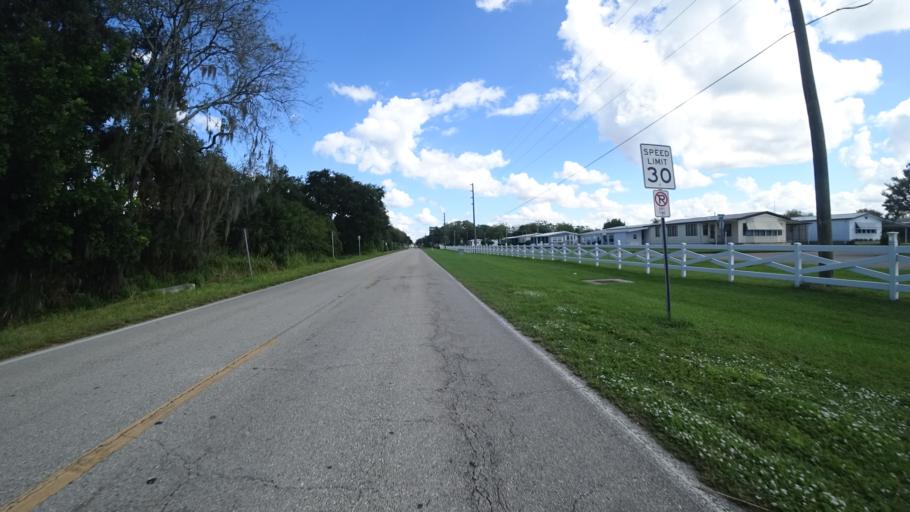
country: US
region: Florida
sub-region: Manatee County
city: Ellenton
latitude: 27.5288
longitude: -82.5178
